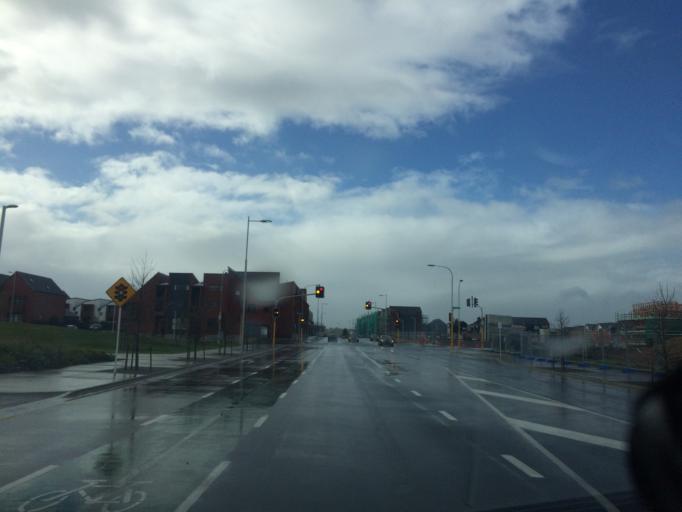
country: NZ
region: Auckland
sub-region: Auckland
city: Rosebank
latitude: -36.7952
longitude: 174.6559
